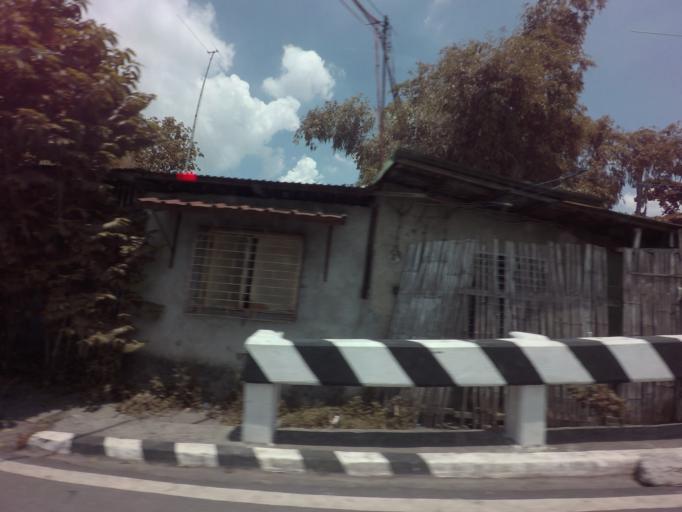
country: PH
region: Calabarzon
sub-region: Province of Laguna
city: San Pedro
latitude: 14.3920
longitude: 121.0505
